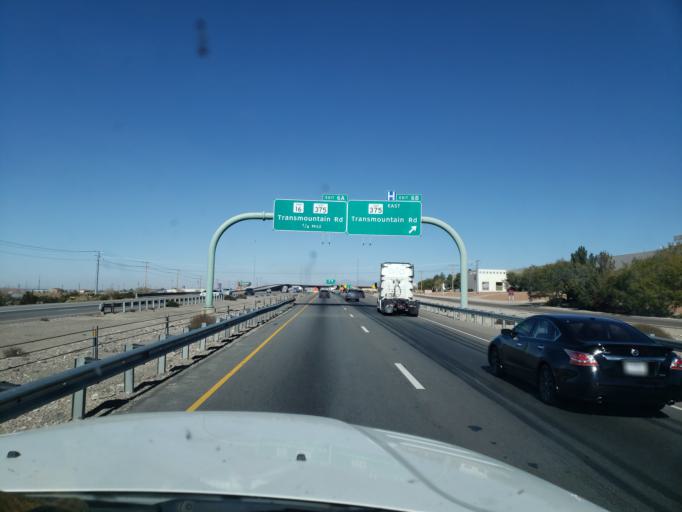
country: US
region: Texas
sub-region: El Paso County
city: Canutillo
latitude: 31.8991
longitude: -106.5827
